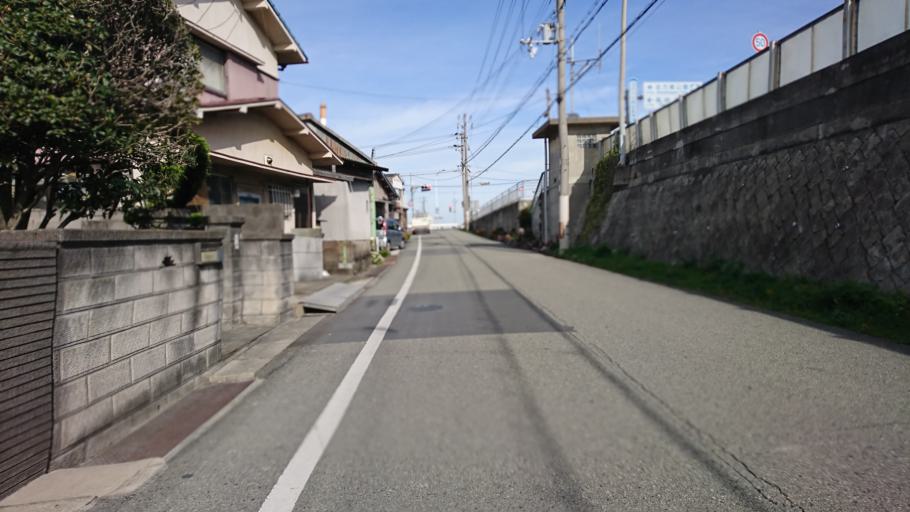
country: JP
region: Hyogo
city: Kakogawacho-honmachi
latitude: 34.7468
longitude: 134.8075
